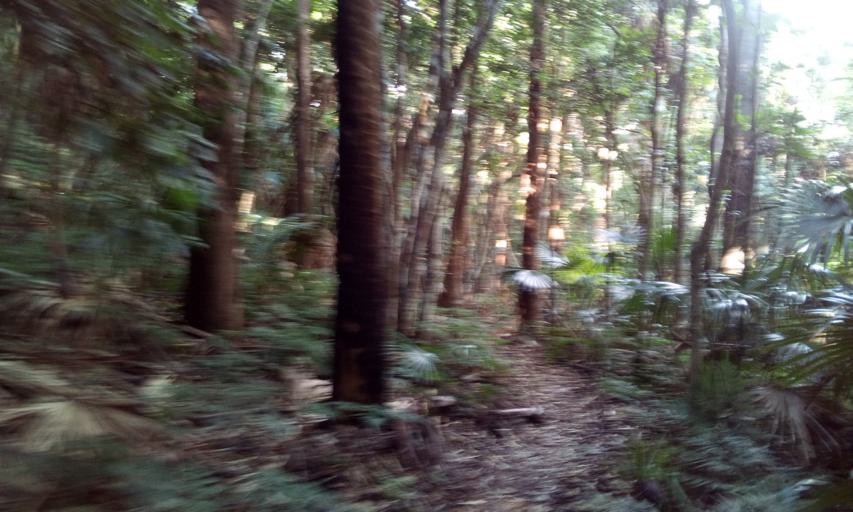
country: AU
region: New South Wales
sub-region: Wollongong
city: Cordeaux Heights
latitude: -34.4428
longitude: 150.7965
